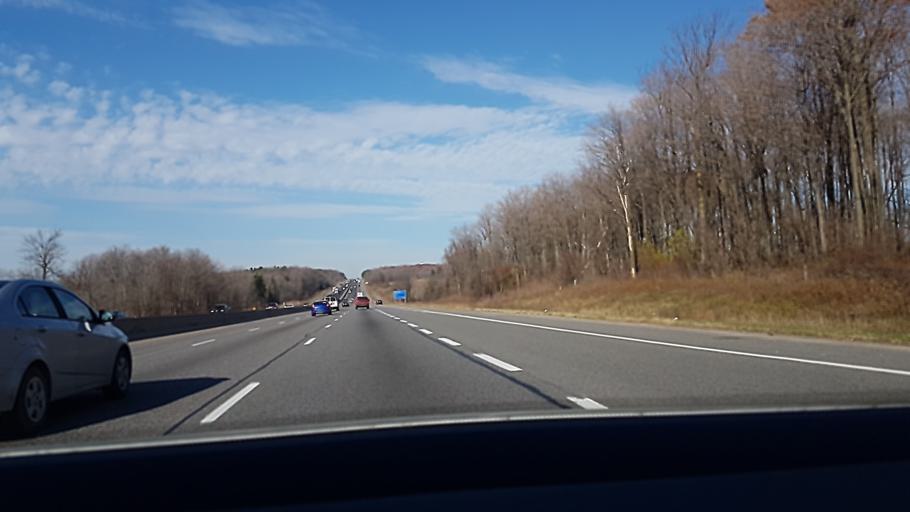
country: CA
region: Ontario
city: Vaughan
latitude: 43.9445
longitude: -79.5717
